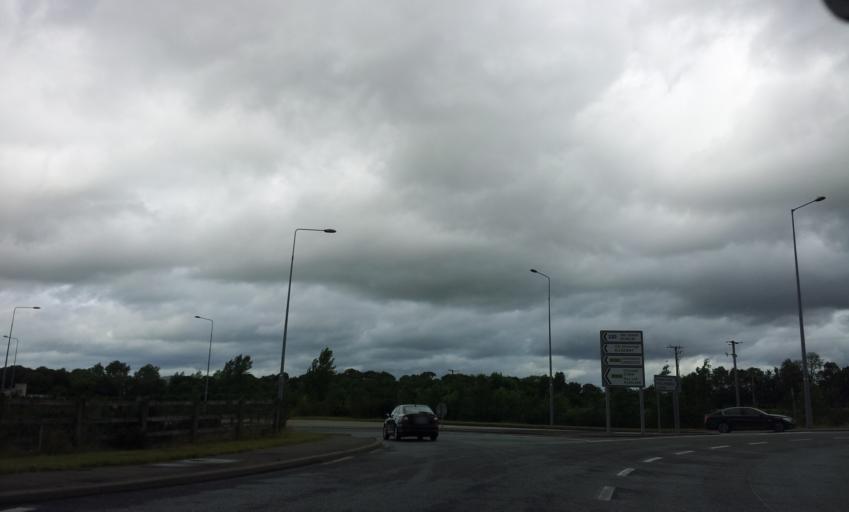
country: IE
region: Munster
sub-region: Waterford
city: Waterford
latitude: 52.2772
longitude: -7.1326
